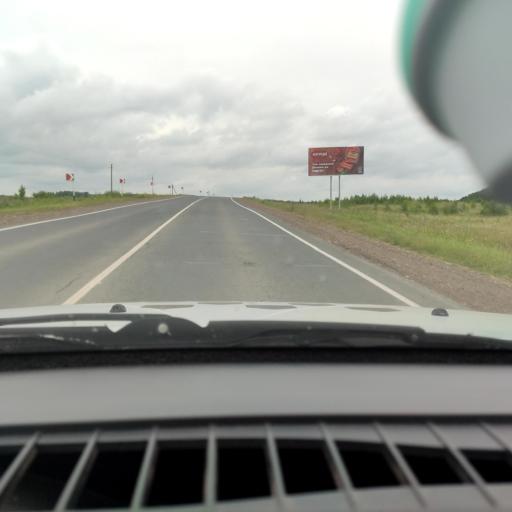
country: RU
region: Perm
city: Kungur
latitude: 57.4459
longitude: 56.9729
